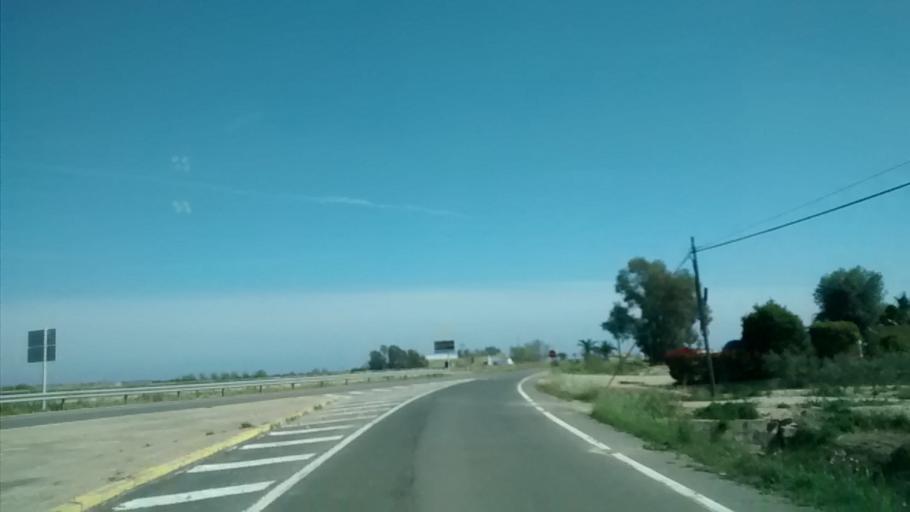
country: ES
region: Catalonia
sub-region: Provincia de Tarragona
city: Deltebre
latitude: 40.7114
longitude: 0.7566
